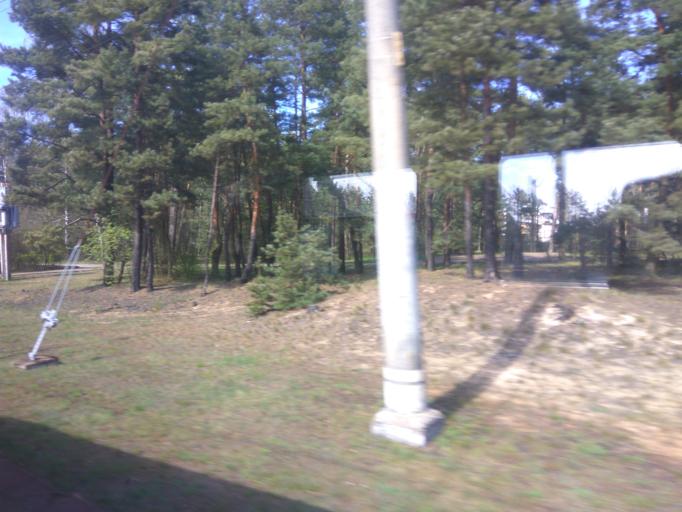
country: LV
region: Babite
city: Pinki
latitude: 56.9712
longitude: 23.8888
